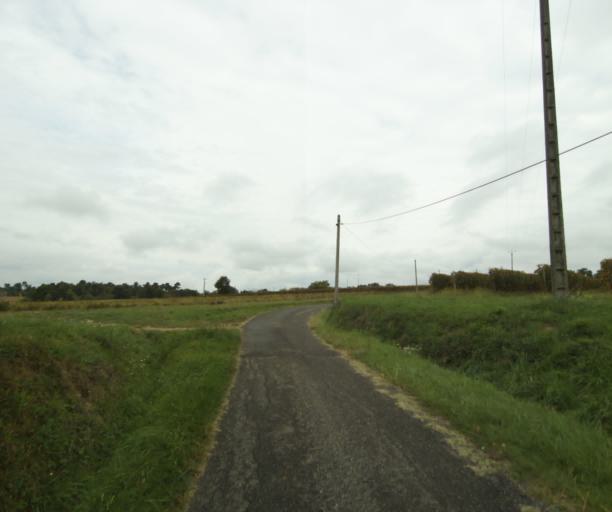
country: FR
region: Midi-Pyrenees
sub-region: Departement du Gers
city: Cazaubon
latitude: 43.8767
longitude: -0.0925
